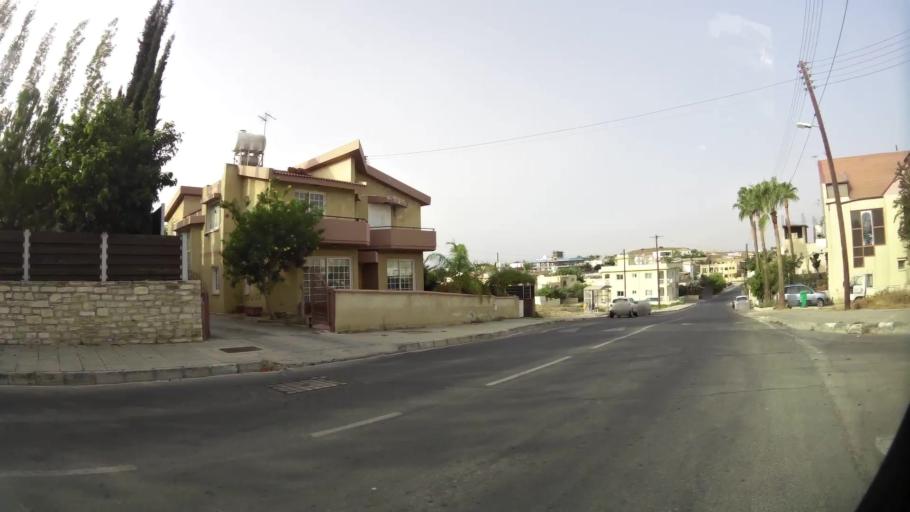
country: CY
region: Lefkosia
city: Geri
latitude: 35.0650
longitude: 33.3894
